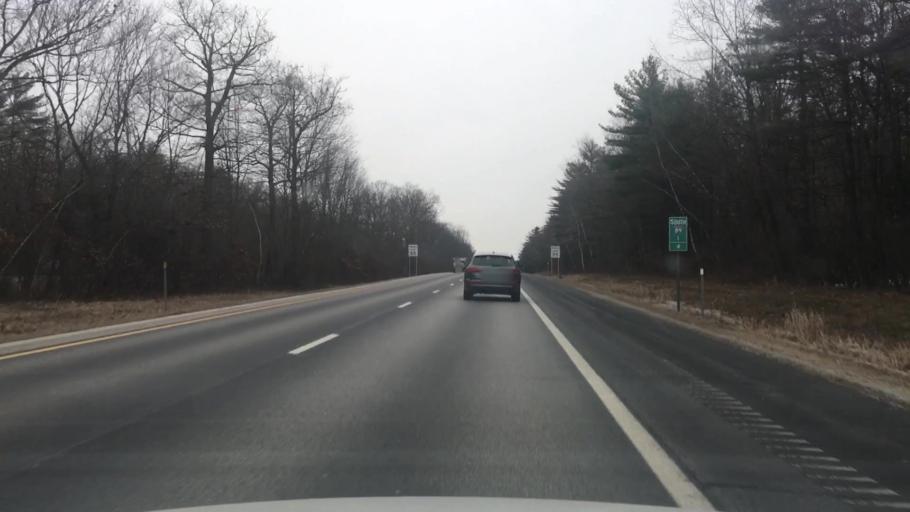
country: US
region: New Hampshire
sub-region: Merrimack County
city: Concord
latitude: 43.1744
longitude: -71.5556
